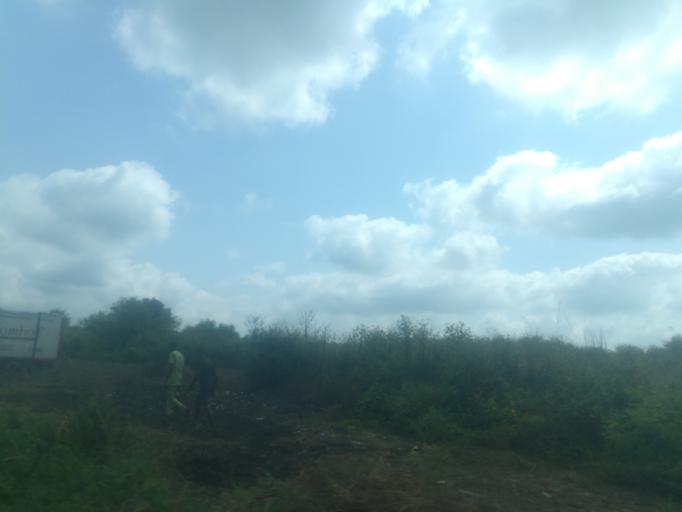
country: NG
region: Oyo
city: Moniya
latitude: 7.5742
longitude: 3.9149
